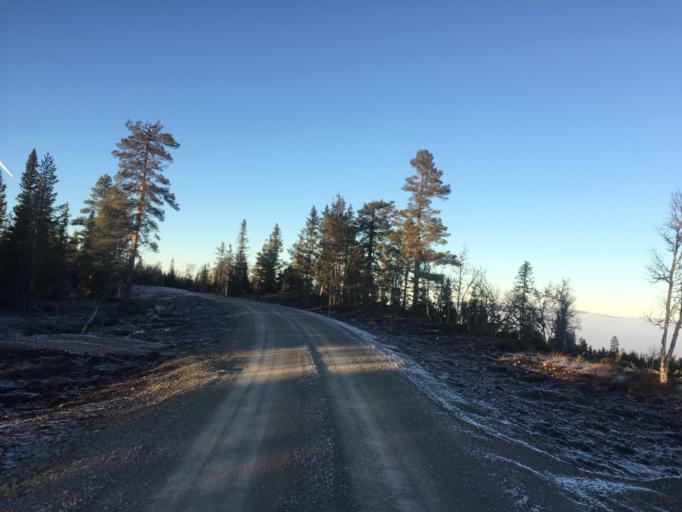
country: NO
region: Hedmark
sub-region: Elverum
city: Elverum
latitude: 61.2096
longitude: 11.7864
